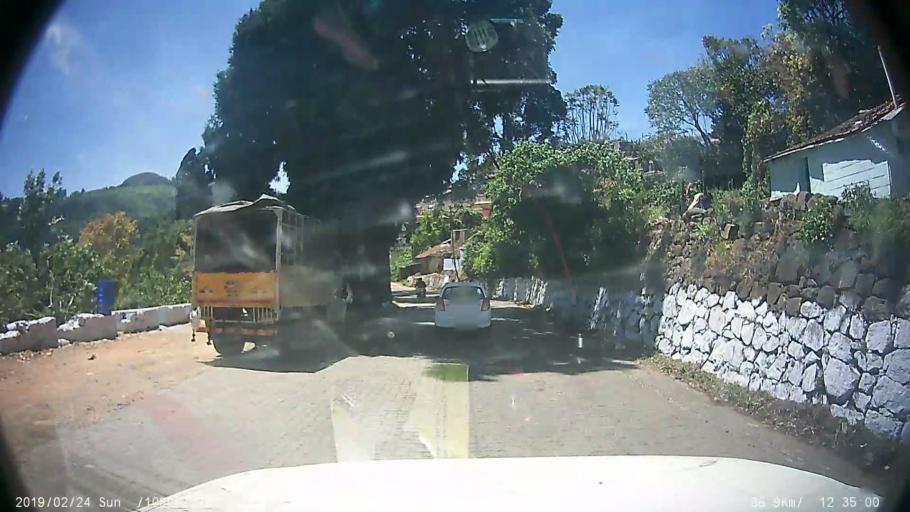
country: IN
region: Tamil Nadu
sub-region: Nilgiri
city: Wellington
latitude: 11.3356
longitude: 76.7989
